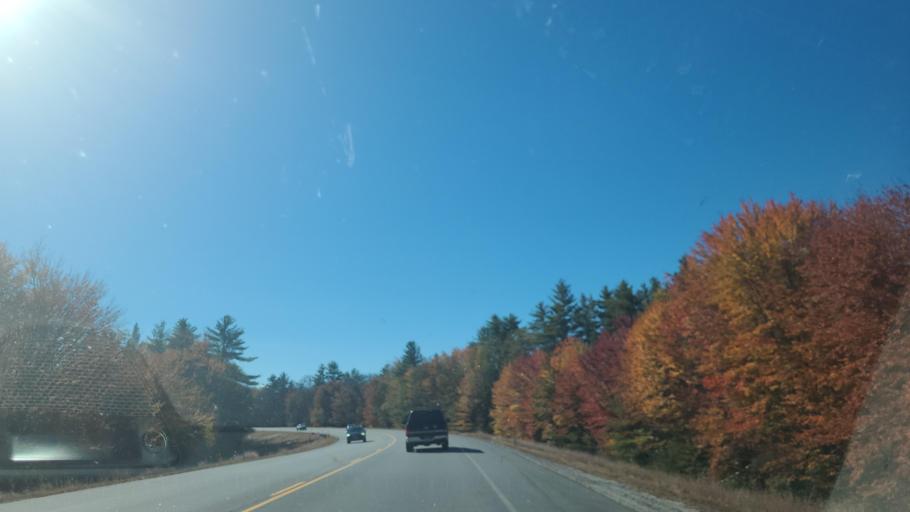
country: US
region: New Hampshire
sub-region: Carroll County
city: Conway
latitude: 43.9997
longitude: -71.0885
